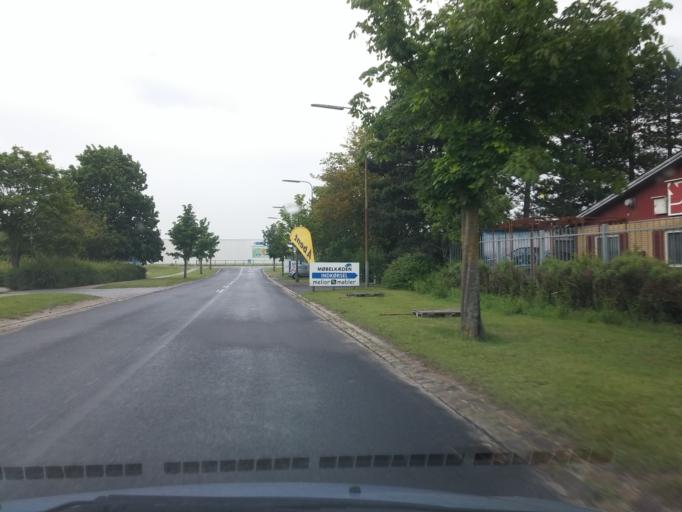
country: DK
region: South Denmark
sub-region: Odense Kommune
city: Odense
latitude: 55.4019
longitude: 10.4183
